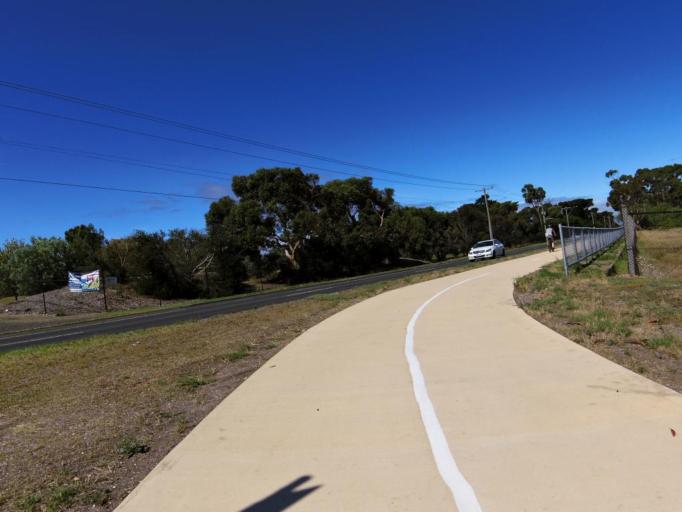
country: AU
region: Victoria
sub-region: Hobsons Bay
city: Altona Meadows
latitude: -37.8760
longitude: 144.7995
